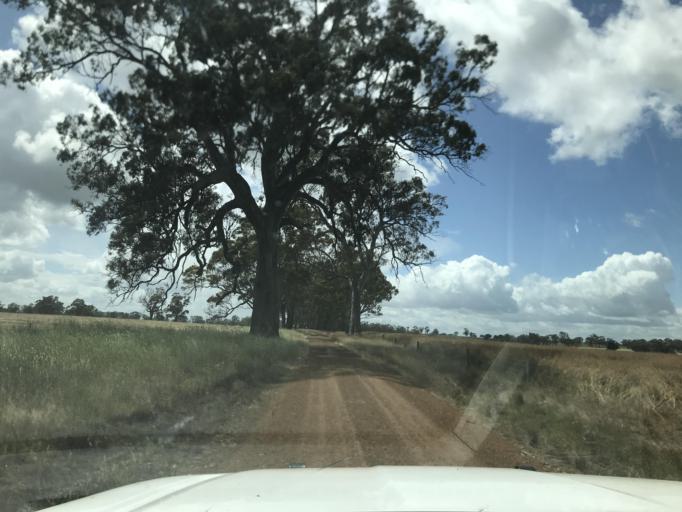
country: AU
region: South Australia
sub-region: Wattle Range
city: Penola
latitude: -37.1845
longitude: 141.4736
